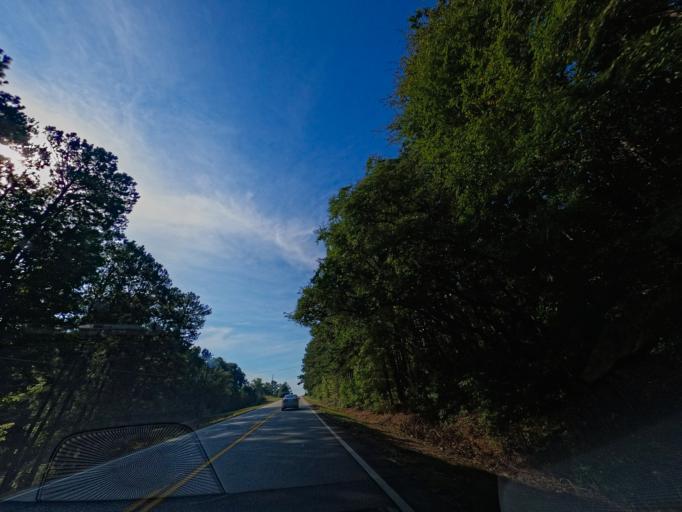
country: US
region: Georgia
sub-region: Troup County
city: Hogansville
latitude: 33.2080
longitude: -84.9226
